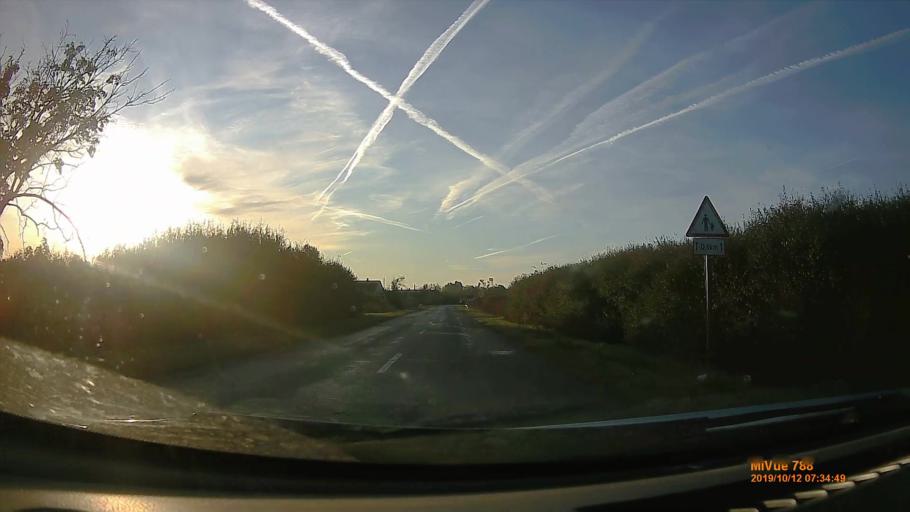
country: HU
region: Hajdu-Bihar
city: Pocsaj
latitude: 47.2585
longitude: 21.8079
